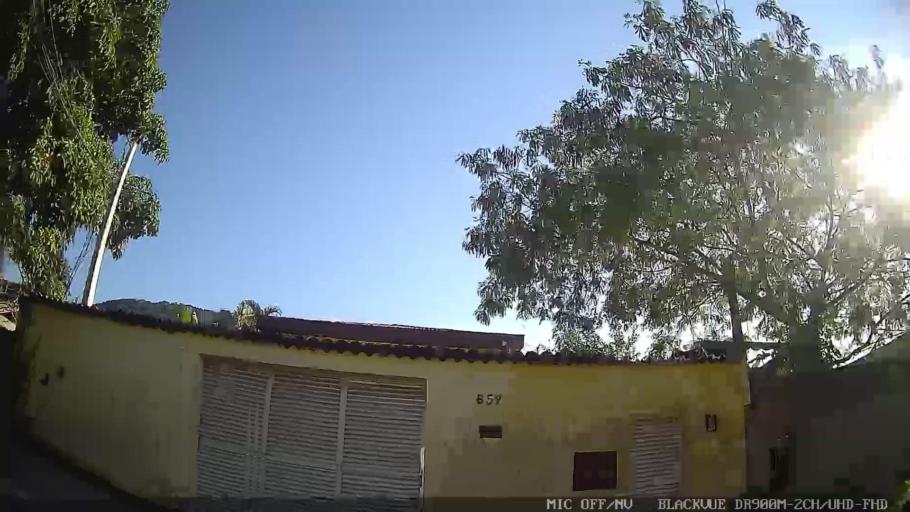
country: BR
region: Sao Paulo
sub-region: Guaruja
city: Guaruja
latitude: -24.0144
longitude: -46.2829
